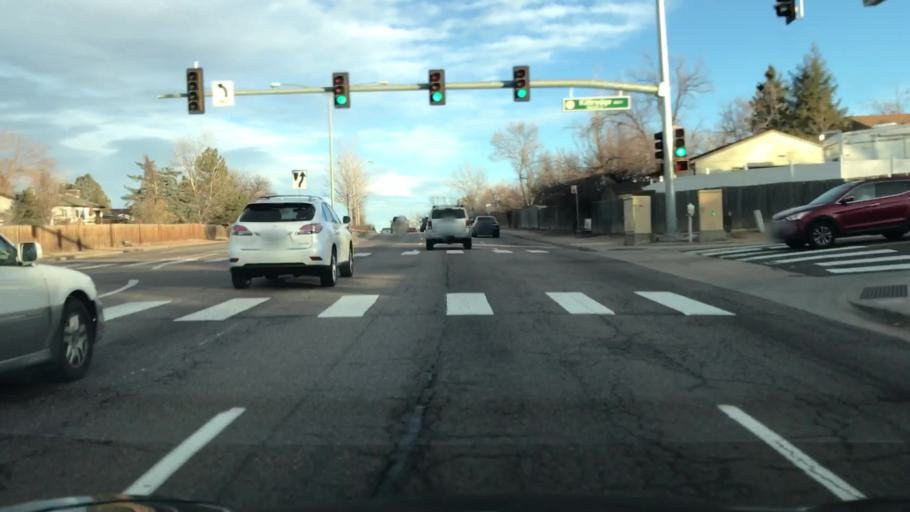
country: US
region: Colorado
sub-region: Adams County
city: Aurora
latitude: 39.6737
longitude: -104.8017
